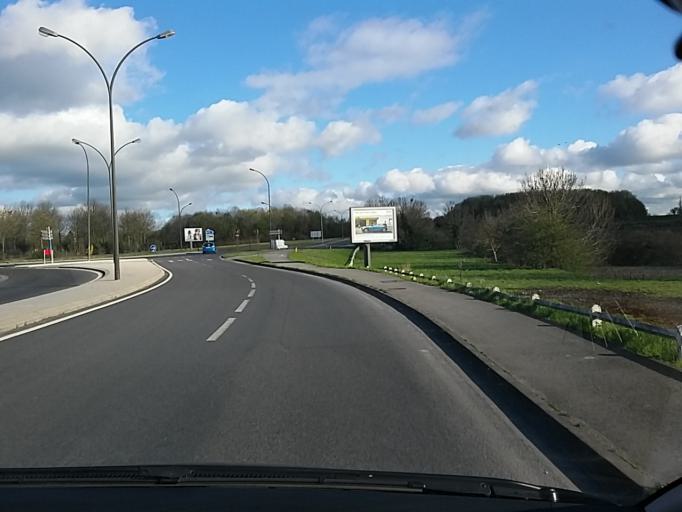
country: FR
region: Picardie
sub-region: Departement de la Somme
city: Amiens
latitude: 49.9264
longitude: 2.2863
